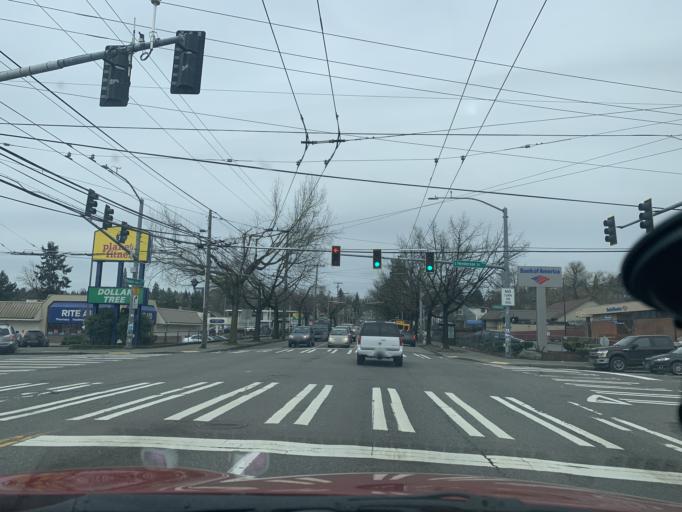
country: US
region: Washington
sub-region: King County
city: Bryn Mawr-Skyway
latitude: 47.5235
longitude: -122.2700
